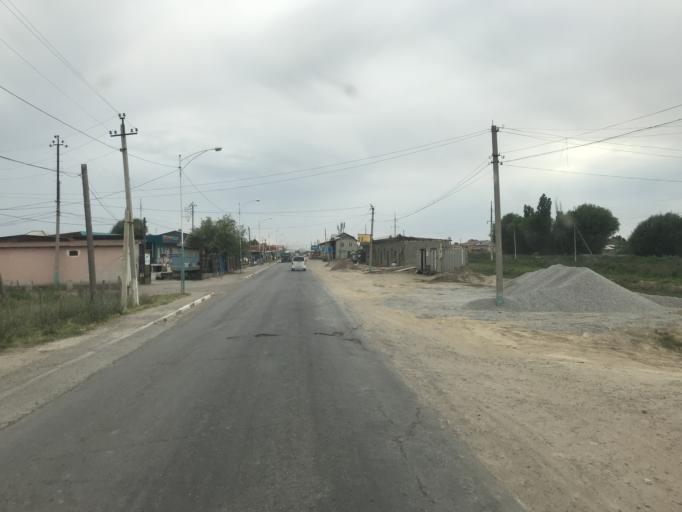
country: KZ
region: Ongtustik Qazaqstan
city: Asykata
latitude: 40.9029
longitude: 68.3619
